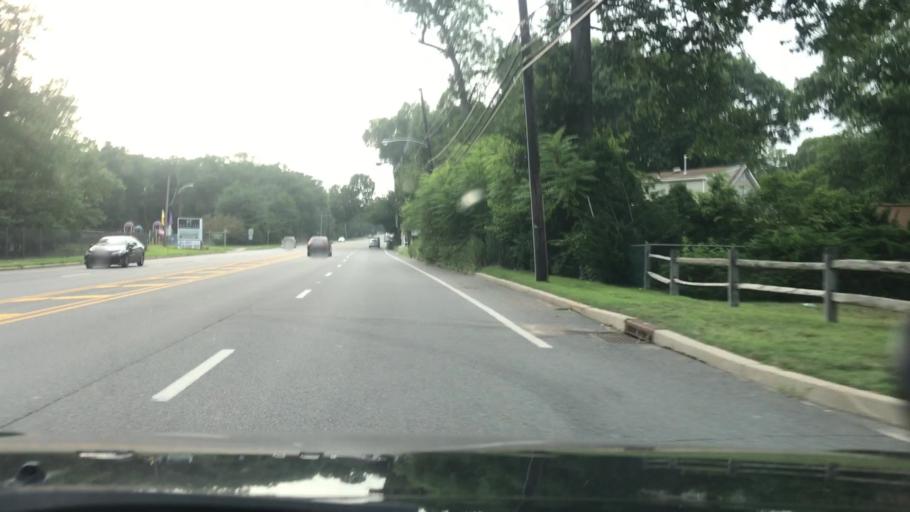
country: US
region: New Jersey
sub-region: Ocean County
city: Lakewood
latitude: 40.1134
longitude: -74.2449
